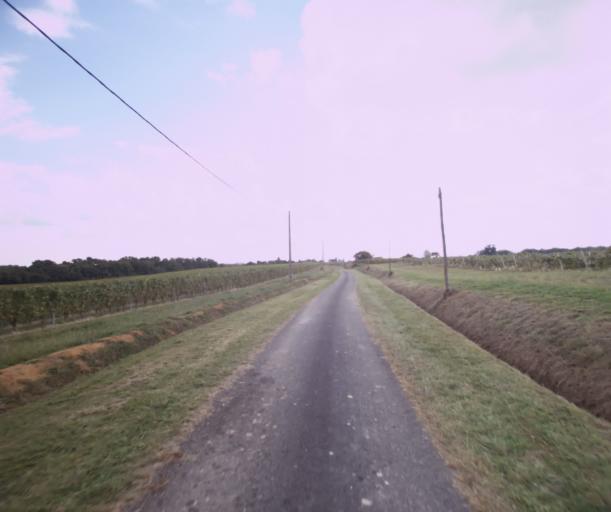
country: FR
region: Midi-Pyrenees
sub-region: Departement du Gers
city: Cazaubon
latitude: 43.8954
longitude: -0.0533
